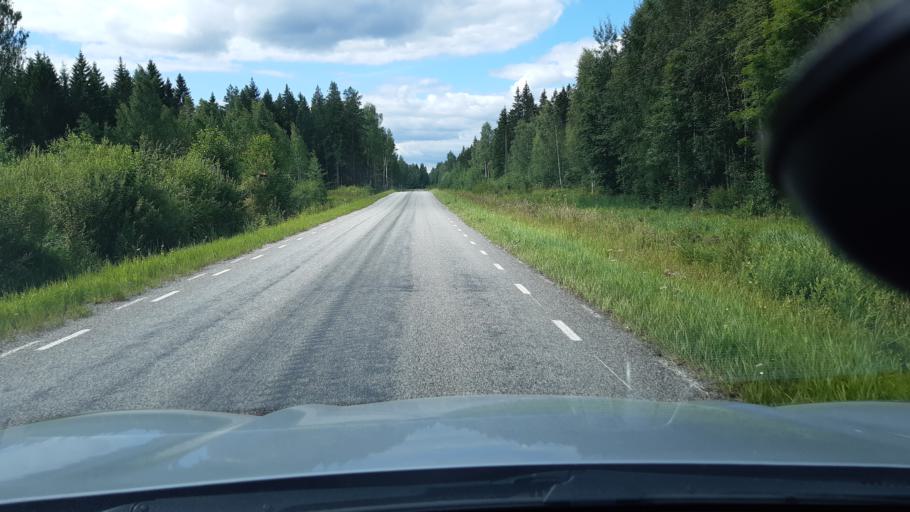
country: EE
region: Raplamaa
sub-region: Jaervakandi vald
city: Jarvakandi
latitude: 58.7992
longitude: 24.8824
